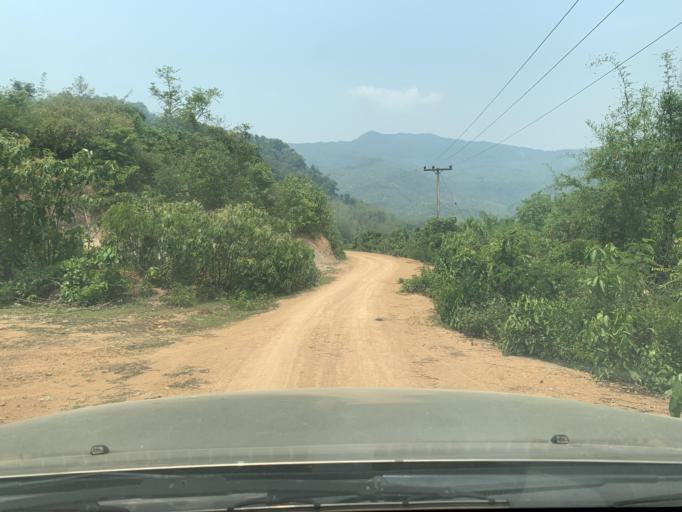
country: LA
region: Louangphabang
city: Louangphabang
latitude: 19.9685
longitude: 102.1267
